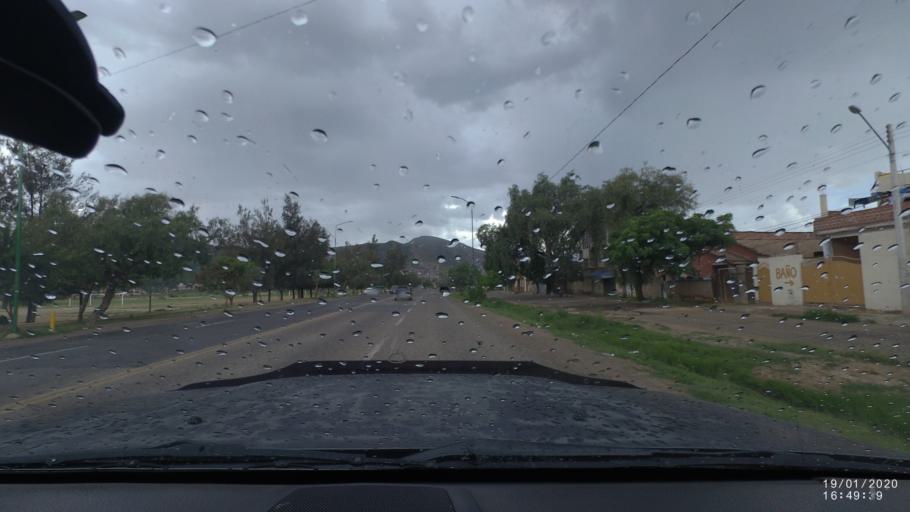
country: BO
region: Cochabamba
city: Cochabamba
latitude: -17.4168
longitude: -66.1391
